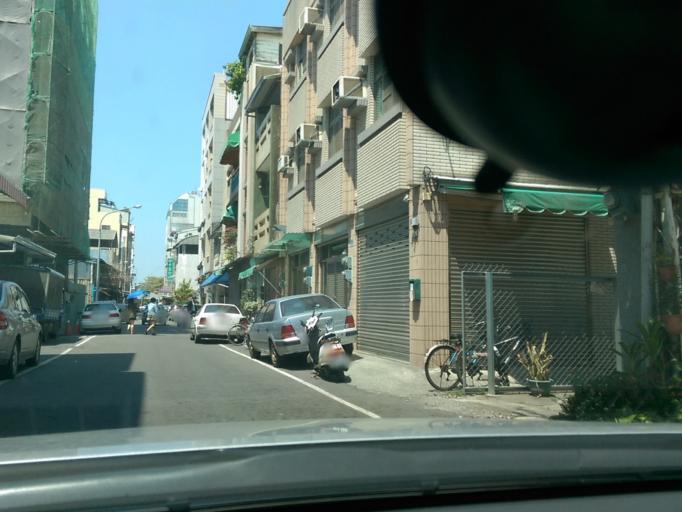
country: TW
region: Taiwan
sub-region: Chiayi
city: Jiayi Shi
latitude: 23.4827
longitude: 120.4501
